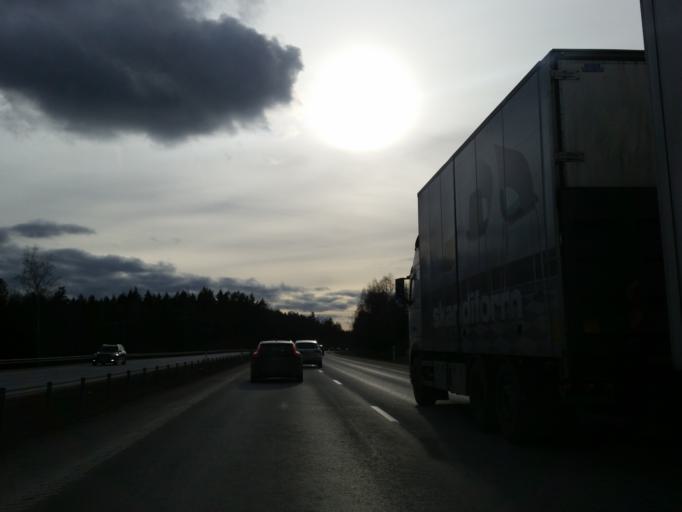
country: SE
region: OEstergoetland
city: Lindo
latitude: 58.6736
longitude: 16.2539
